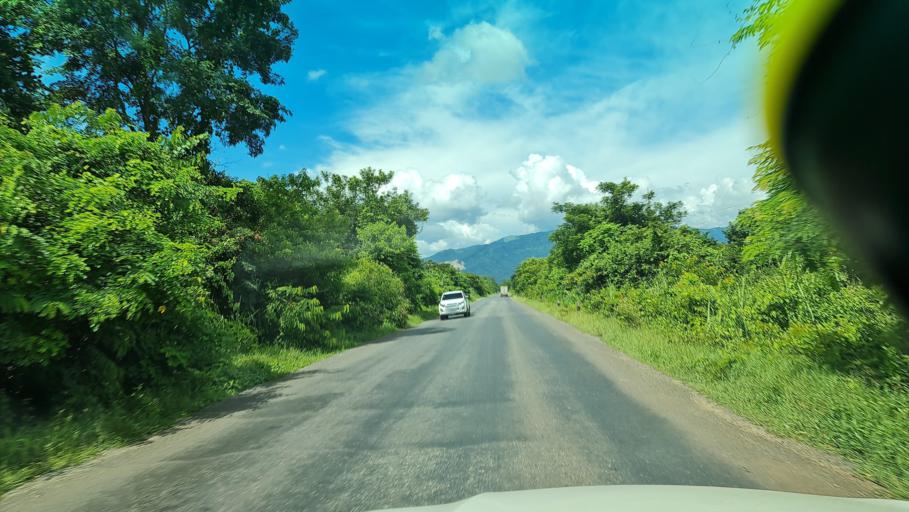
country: LA
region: Bolikhamxai
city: Pakkading
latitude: 18.2938
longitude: 104.0850
